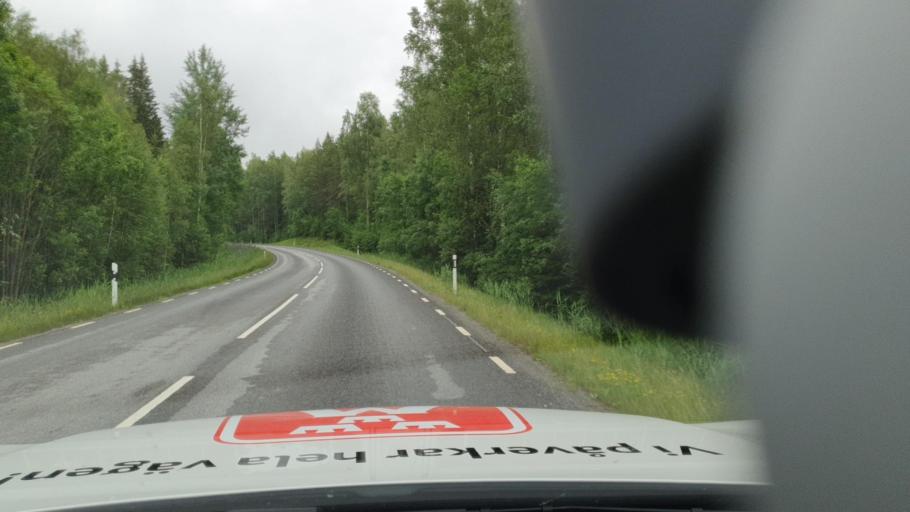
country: SE
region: OErebro
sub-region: Degerfors Kommun
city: Degerfors
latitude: 59.2292
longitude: 14.4140
